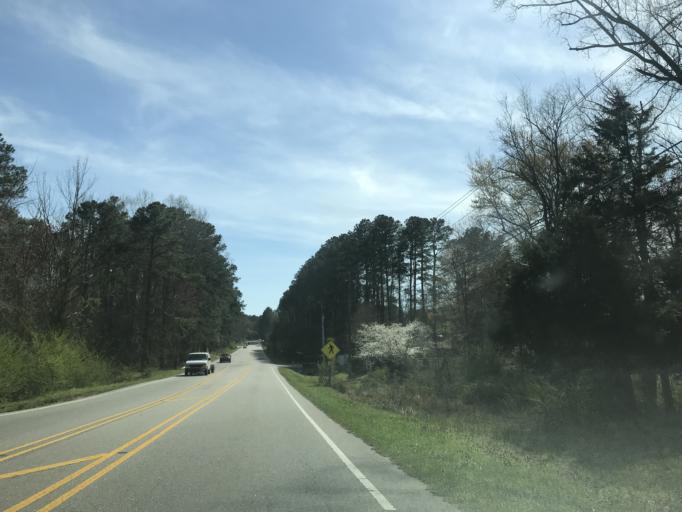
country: US
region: North Carolina
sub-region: Wake County
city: Knightdale
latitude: 35.8398
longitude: -78.5426
